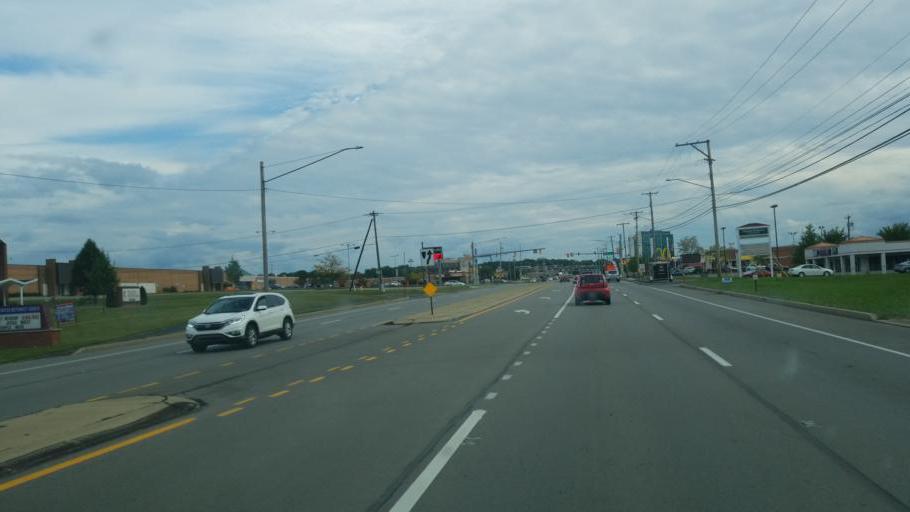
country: US
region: Pennsylvania
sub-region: Mercer County
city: Hermitage
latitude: 41.2372
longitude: -80.4499
